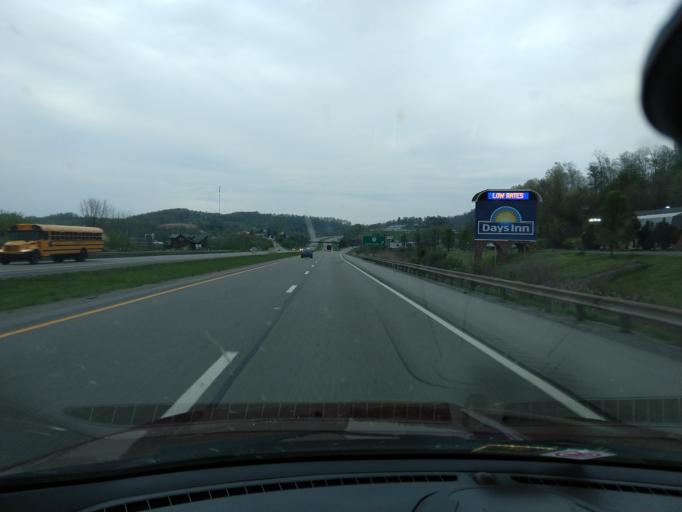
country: US
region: West Virginia
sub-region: Lewis County
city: Weston
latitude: 39.0981
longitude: -80.3920
